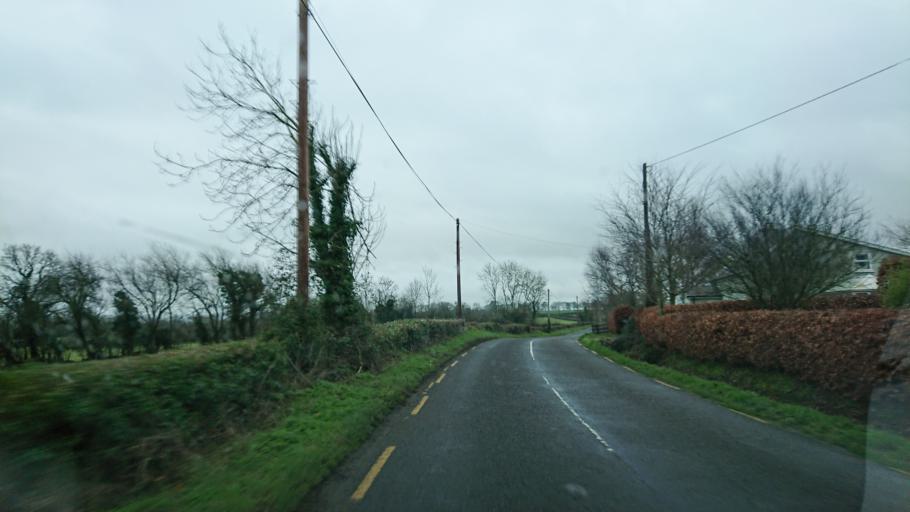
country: IE
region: Leinster
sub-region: Kilkenny
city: Callan
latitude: 52.5333
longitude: -7.2933
